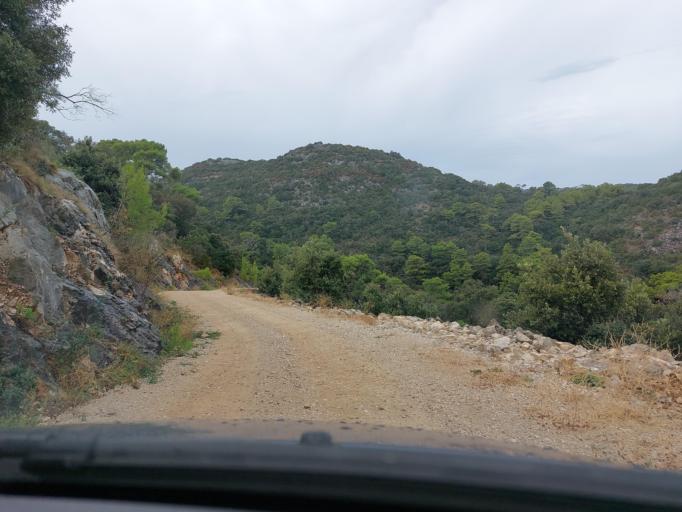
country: HR
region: Dubrovacko-Neretvanska
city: Smokvica
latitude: 42.7486
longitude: 16.9150
